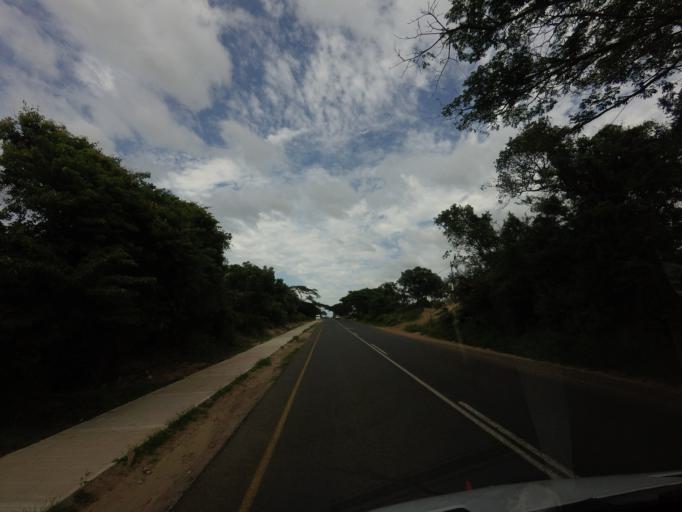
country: ZA
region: KwaZulu-Natal
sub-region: uMkhanyakude District Municipality
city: Mtubatuba
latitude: -28.3774
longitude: 32.3713
